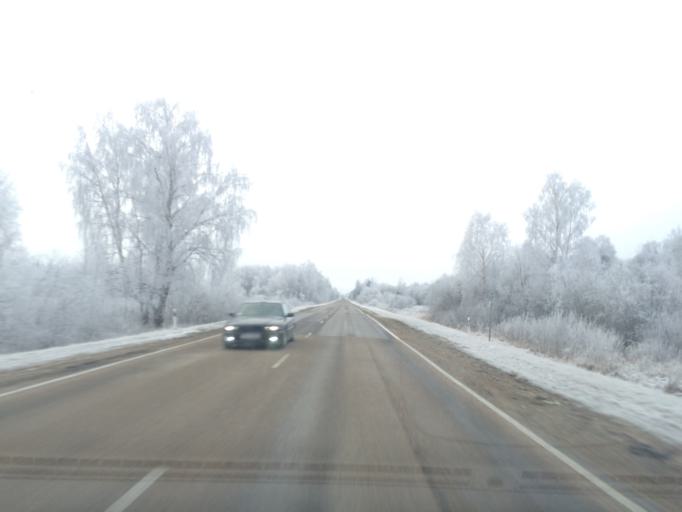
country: LV
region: Rezekne
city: Rezekne
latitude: 56.6501
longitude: 27.4957
